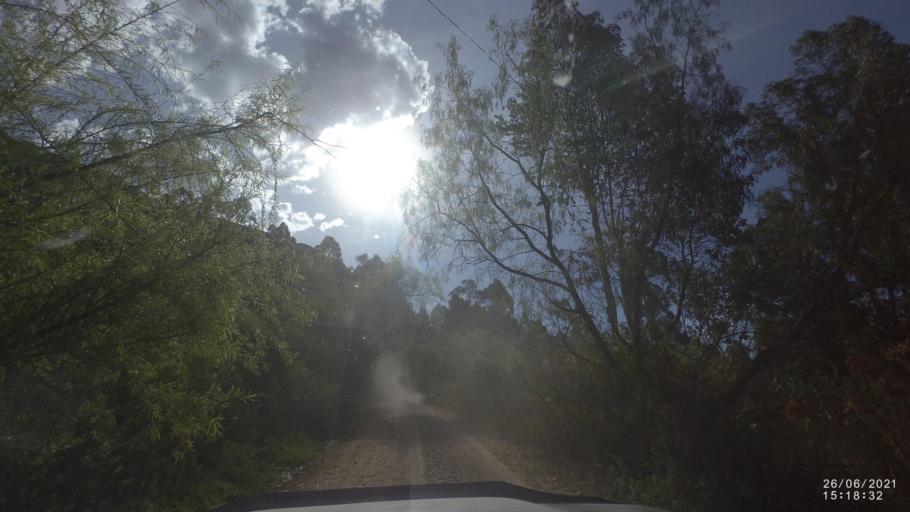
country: BO
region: Cochabamba
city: Mizque
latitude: -17.9498
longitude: -65.6567
